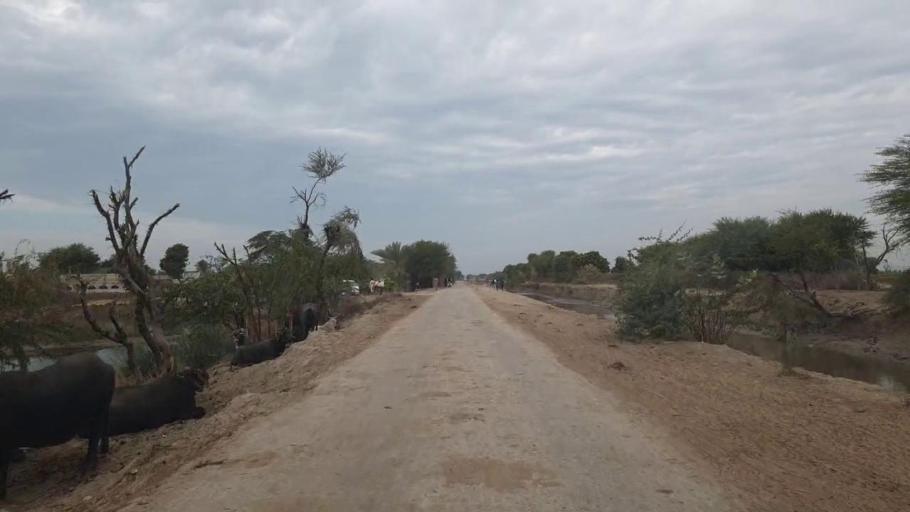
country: PK
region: Sindh
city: Jhol
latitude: 25.9852
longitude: 68.9006
